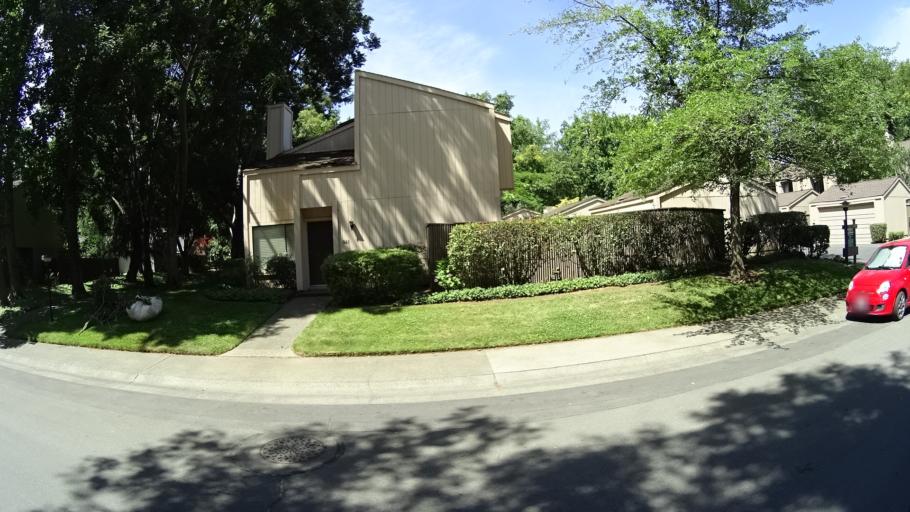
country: US
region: California
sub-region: Sacramento County
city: Rosemont
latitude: 38.5648
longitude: -121.4157
